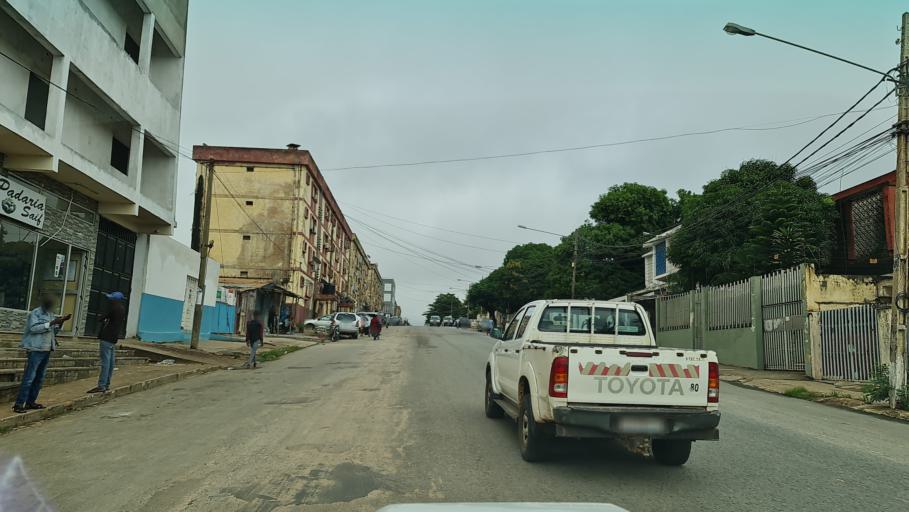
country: MZ
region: Nampula
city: Nampula
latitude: -15.1310
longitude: 39.2679
